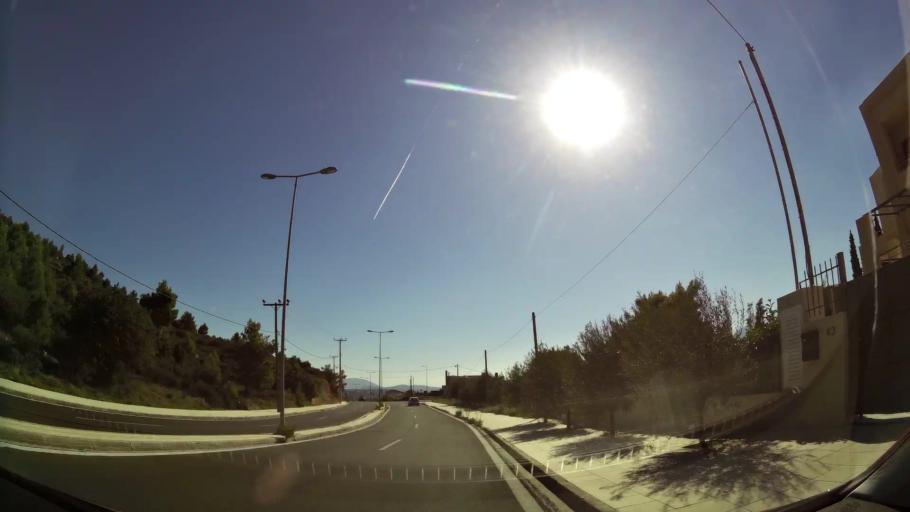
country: GR
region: Attica
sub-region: Nomarchia Anatolikis Attikis
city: Dhrafi
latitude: 38.0151
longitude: 23.9111
